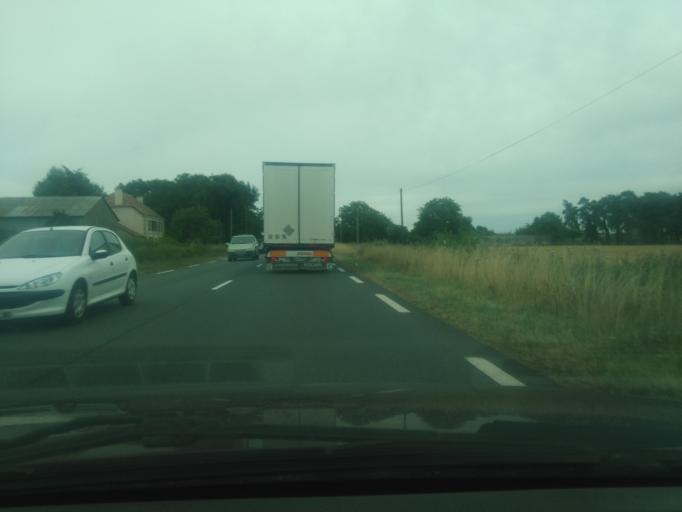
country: FR
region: Poitou-Charentes
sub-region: Departement de la Vienne
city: Lavoux
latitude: 46.5621
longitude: 0.5542
